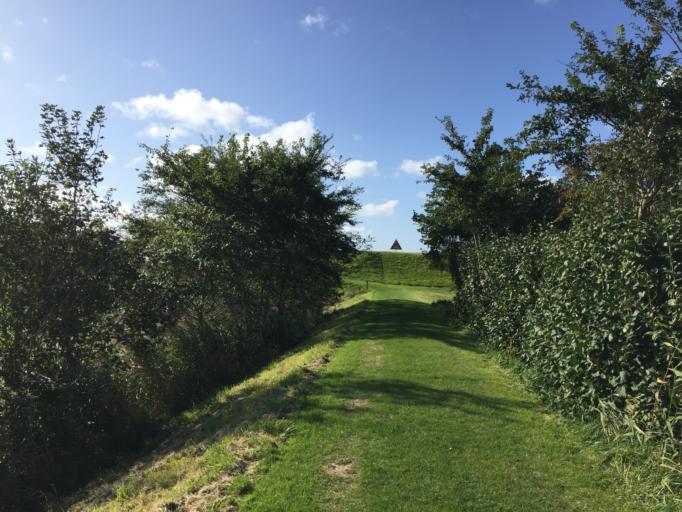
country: DE
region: Schleswig-Holstein
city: Klanxbull
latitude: 54.9566
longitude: 8.6836
